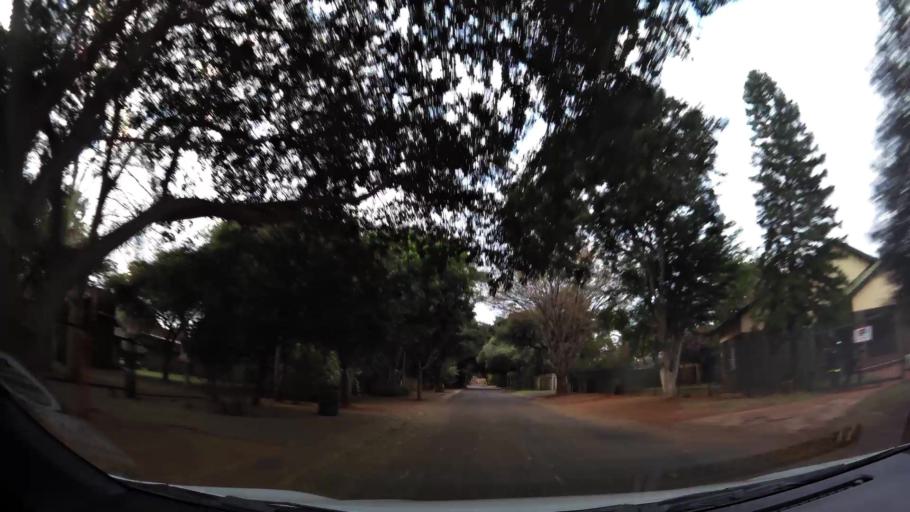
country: ZA
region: Limpopo
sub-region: Waterberg District Municipality
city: Mokopane
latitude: -24.2022
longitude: 29.0040
